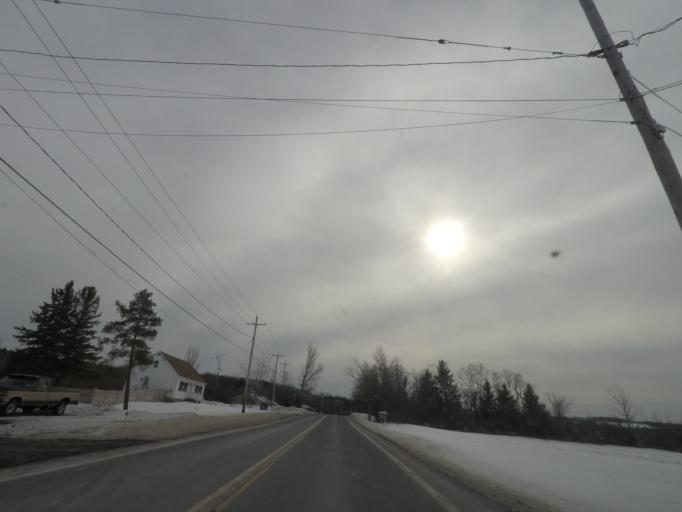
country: US
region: New York
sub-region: Albany County
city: Altamont
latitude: 42.6873
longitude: -74.0698
